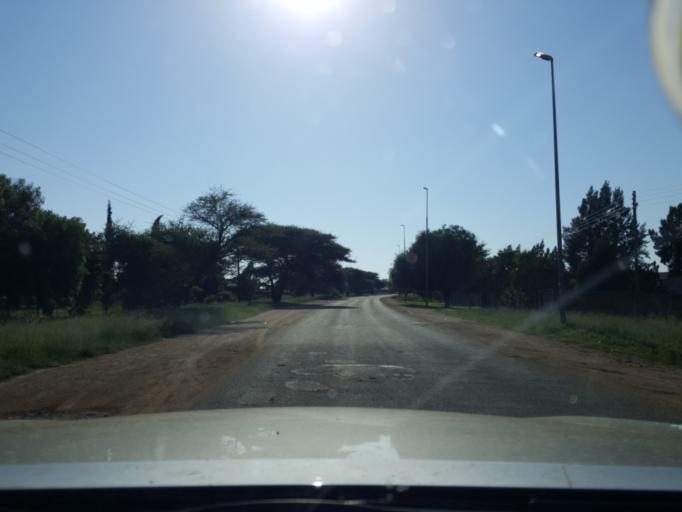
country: ZA
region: North-West
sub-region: Ngaka Modiri Molema District Municipality
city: Mmabatho
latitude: -25.8257
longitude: 25.6404
